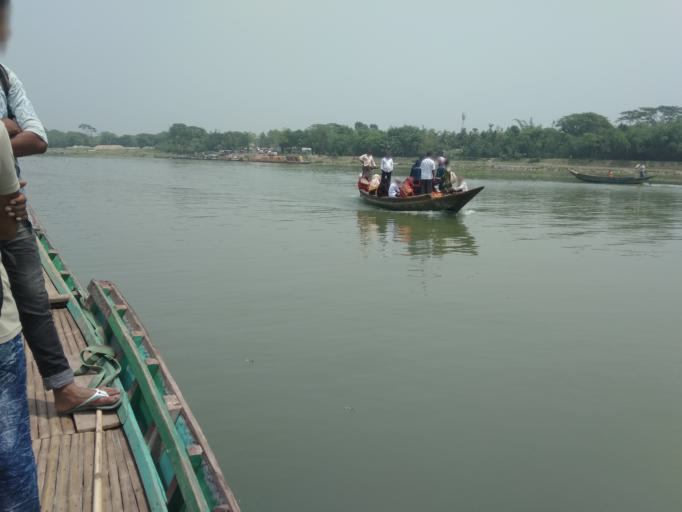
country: BD
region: Khulna
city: Kalia
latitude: 23.1945
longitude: 89.6908
